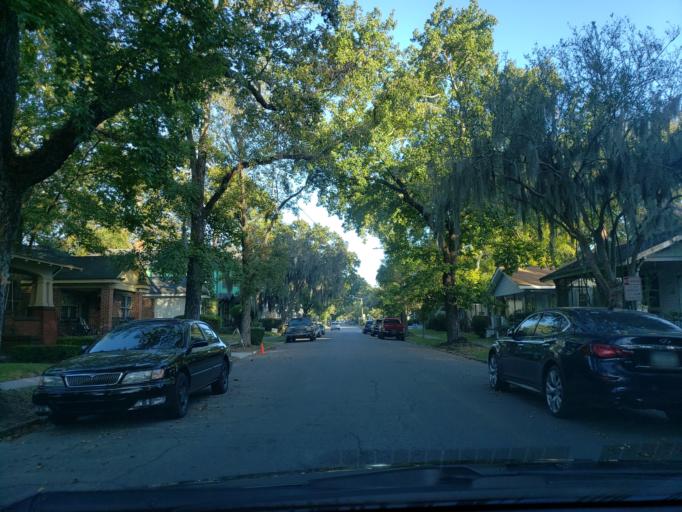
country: US
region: Georgia
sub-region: Chatham County
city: Savannah
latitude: 32.0552
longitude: -81.0881
